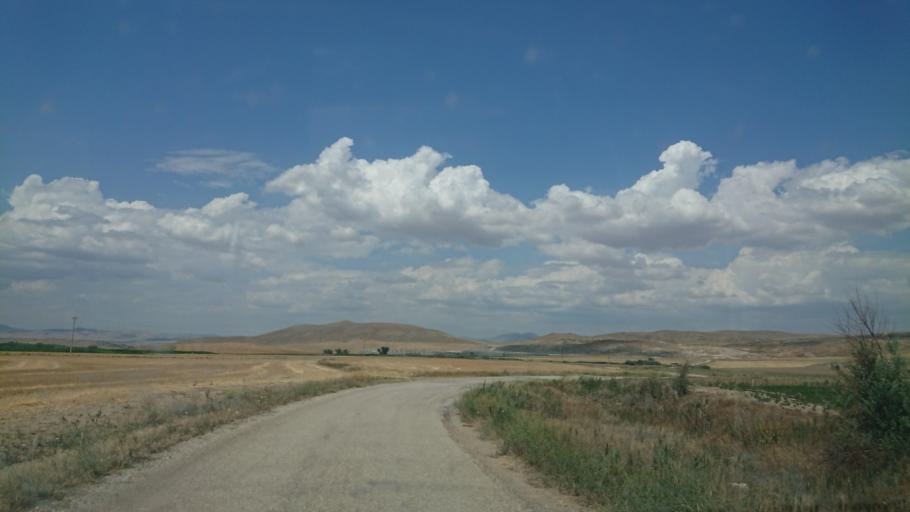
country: TR
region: Aksaray
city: Sariyahsi
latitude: 38.9877
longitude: 33.9083
